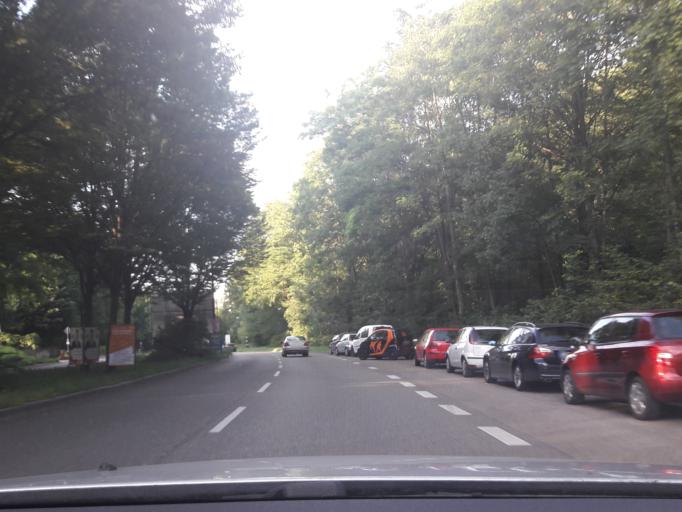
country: DE
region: Baden-Wuerttemberg
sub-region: Regierungsbezirk Stuttgart
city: Ludwigsburg
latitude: 48.9043
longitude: 9.2130
